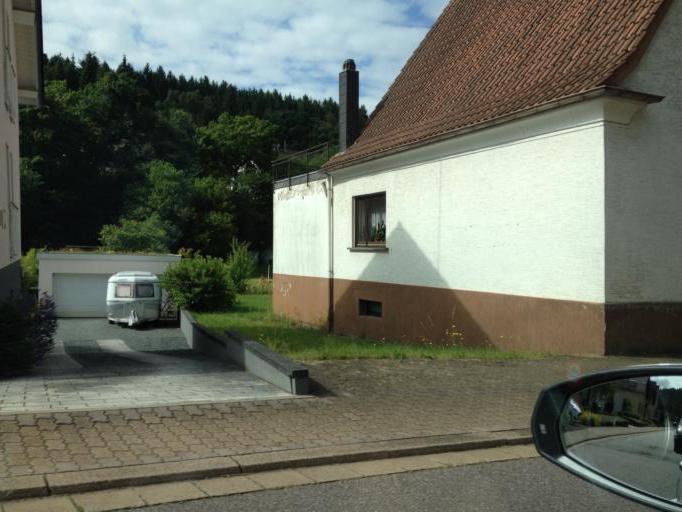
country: DE
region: Saarland
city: Mettlach
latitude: 49.4937
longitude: 6.6149
